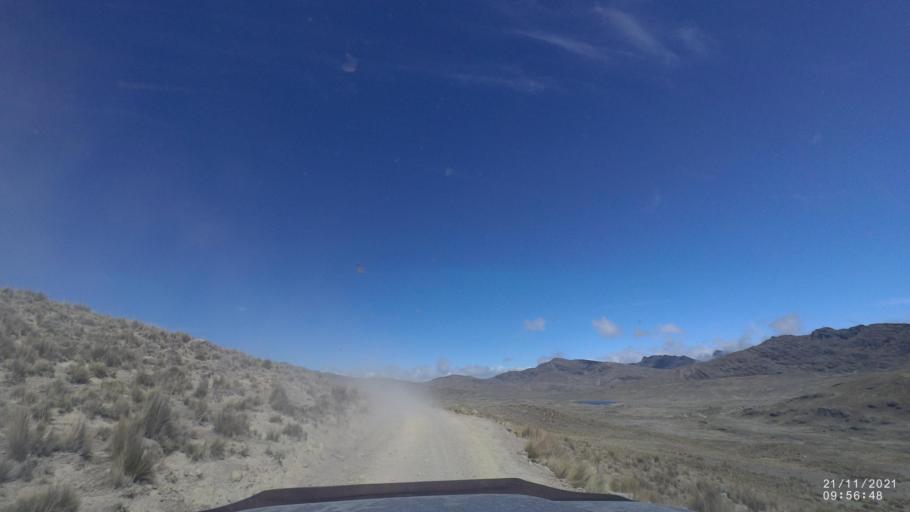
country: BO
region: Cochabamba
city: Cochabamba
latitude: -17.0407
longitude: -66.2673
